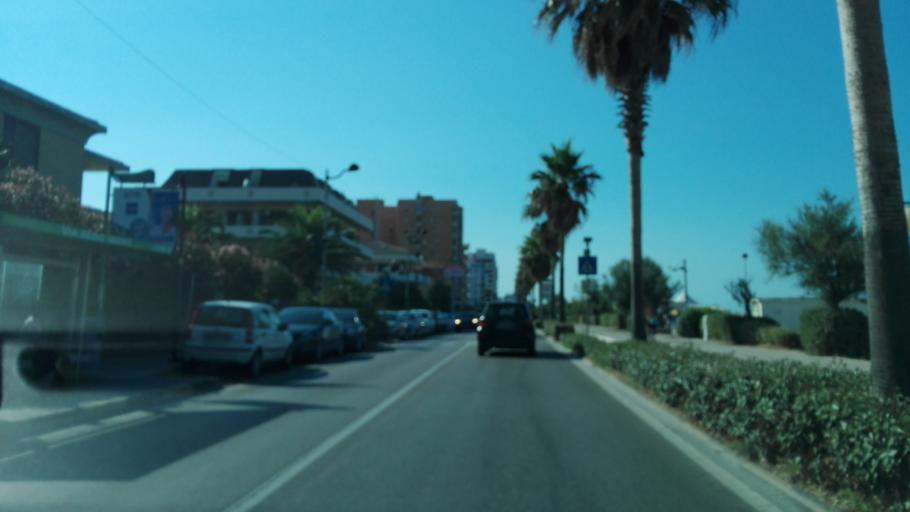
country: IT
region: Abruzzo
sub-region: Provincia di Pescara
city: Montesilvano Marina
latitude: 42.5138
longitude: 14.1651
